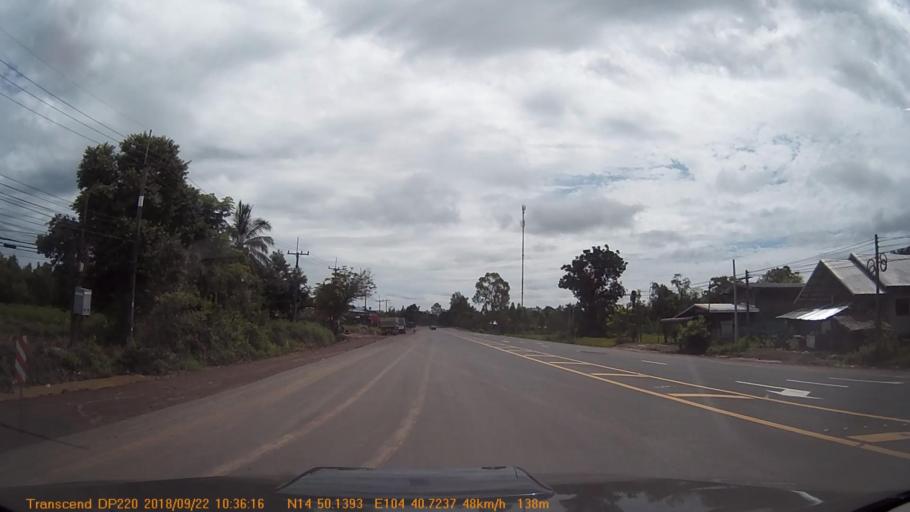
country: TH
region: Sisaket
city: Benchalak
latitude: 14.8359
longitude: 104.6788
